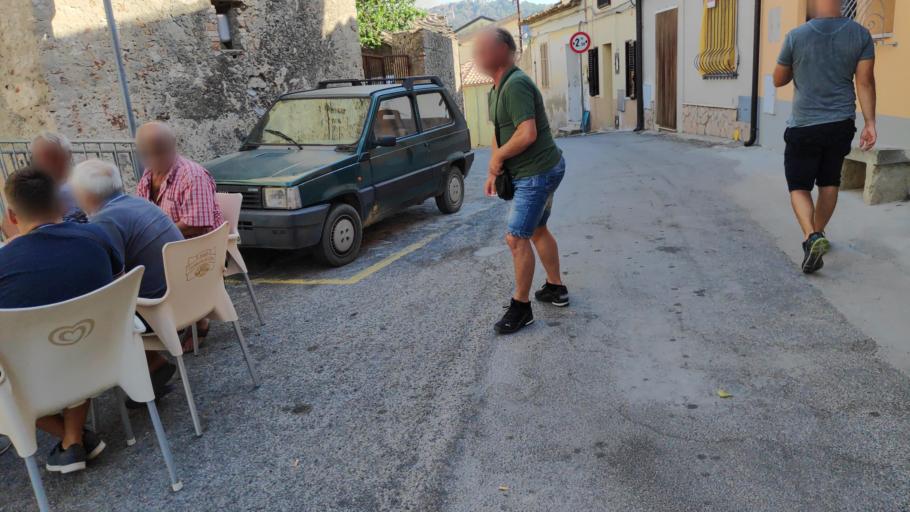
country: IT
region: Calabria
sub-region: Provincia di Catanzaro
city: San Floro
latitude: 38.8376
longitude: 16.5206
